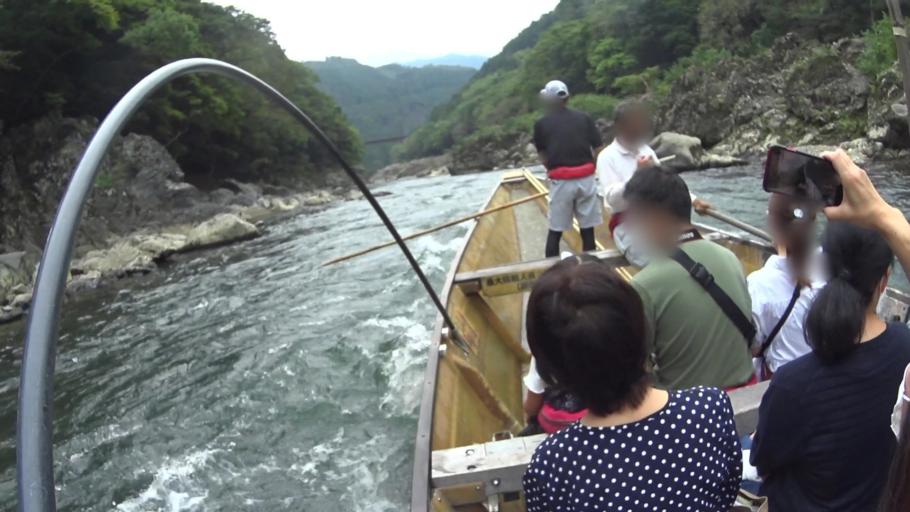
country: JP
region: Kyoto
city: Kameoka
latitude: 35.0185
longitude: 135.6258
